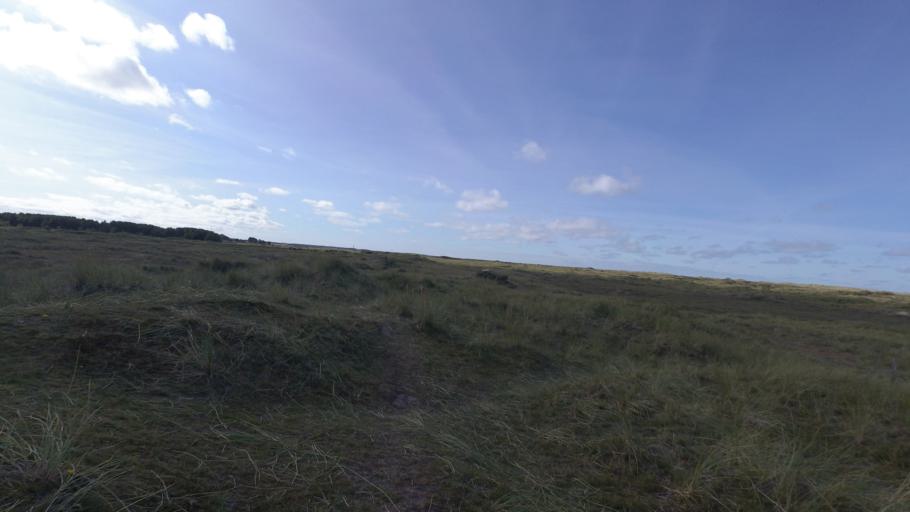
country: NL
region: Friesland
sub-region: Gemeente Ameland
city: Hollum
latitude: 53.4550
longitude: 5.7024
